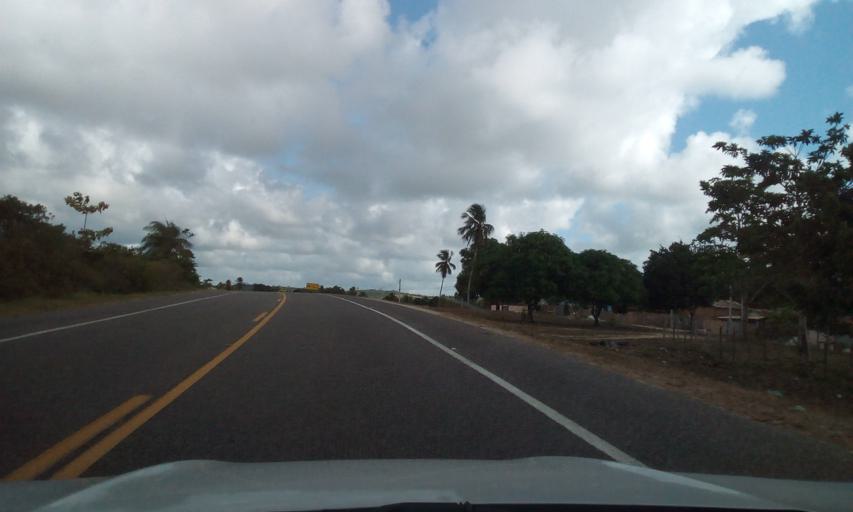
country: BR
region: Bahia
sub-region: Conde
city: Conde
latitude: -11.7983
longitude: -37.6271
